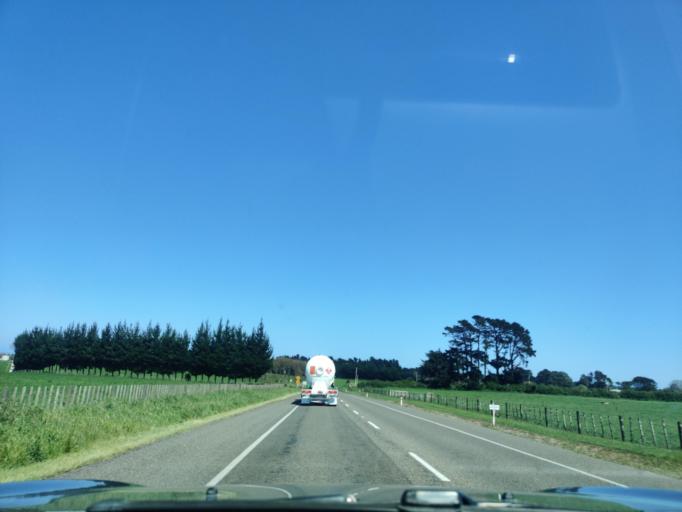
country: NZ
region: Manawatu-Wanganui
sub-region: Wanganui District
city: Wanganui
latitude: -39.8227
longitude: 174.8514
